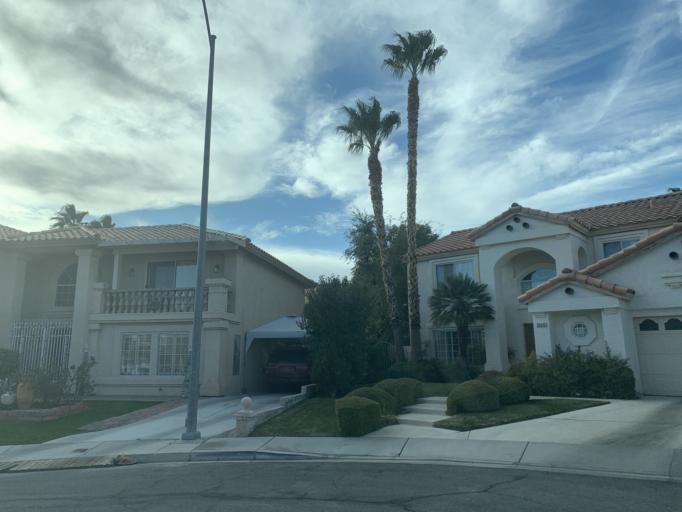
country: US
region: Nevada
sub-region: Clark County
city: Summerlin South
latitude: 36.1294
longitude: -115.3017
